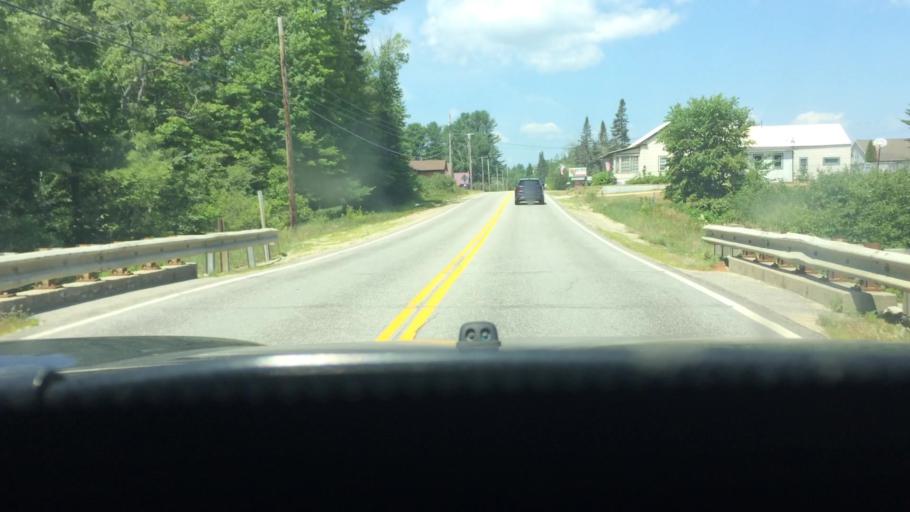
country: US
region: Maine
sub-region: Oxford County
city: Oxford
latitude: 44.1327
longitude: -70.4494
